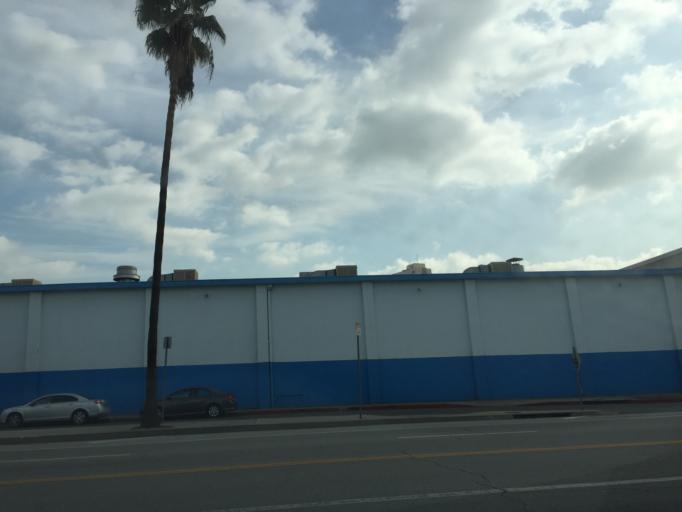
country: US
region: California
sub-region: Los Angeles County
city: Boyle Heights
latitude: 34.0635
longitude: -118.2106
